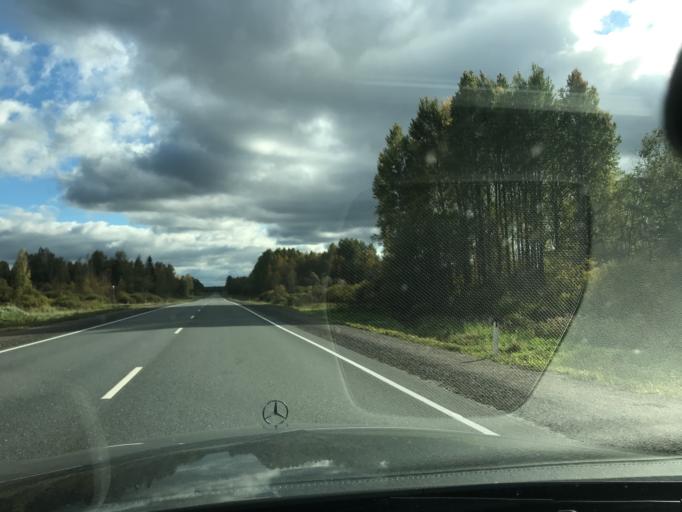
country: RU
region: Pskov
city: Pushkinskiye Gory
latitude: 57.0332
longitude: 28.5963
